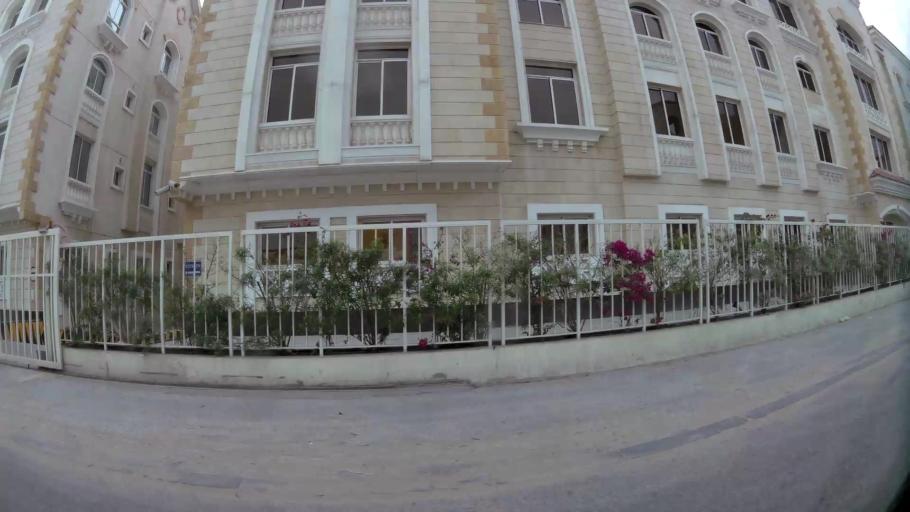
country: QA
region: Baladiyat ad Dawhah
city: Doha
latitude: 25.2761
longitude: 51.4944
